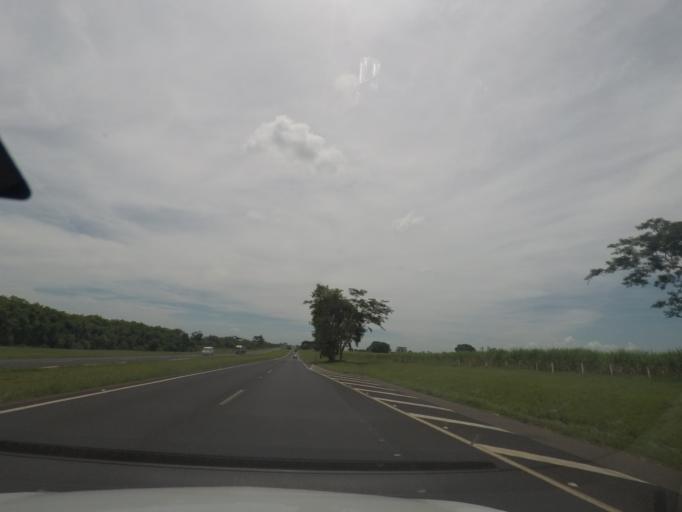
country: BR
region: Sao Paulo
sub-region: Bebedouro
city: Bebedouro
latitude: -20.9876
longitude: -48.4346
